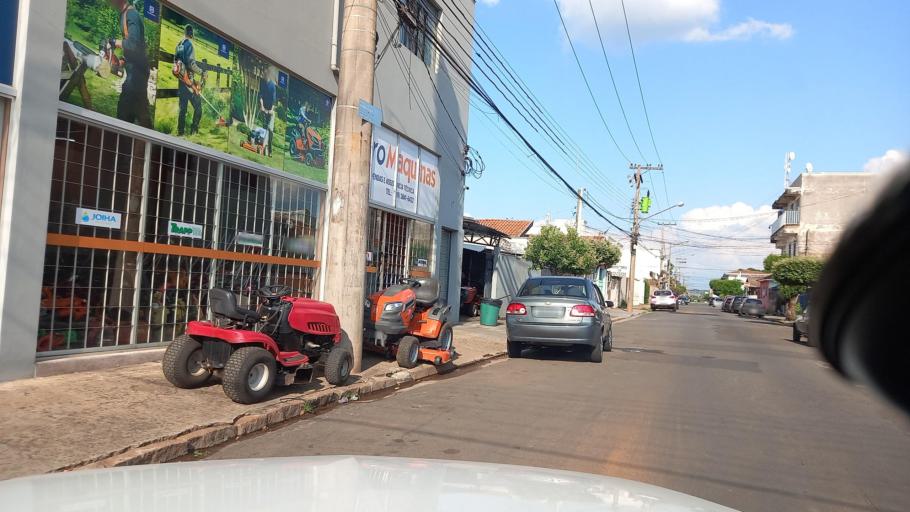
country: BR
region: Sao Paulo
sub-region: Moji-Guacu
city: Mogi-Gaucu
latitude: -22.3527
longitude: -46.9455
